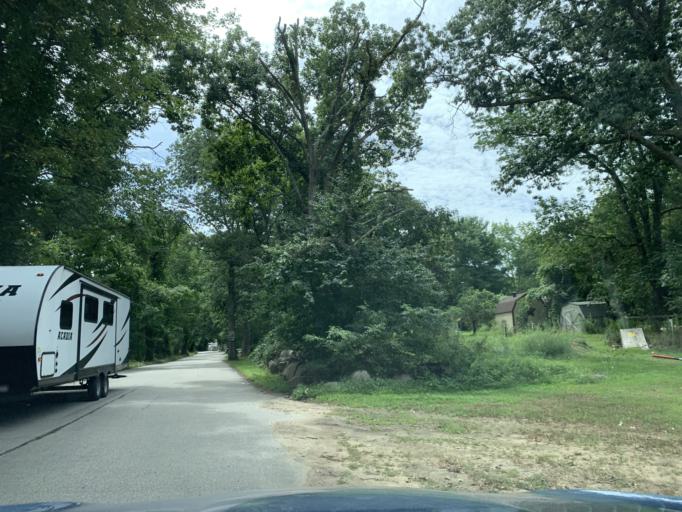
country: US
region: Rhode Island
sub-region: Washington County
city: Exeter
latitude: 41.5584
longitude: -71.6222
